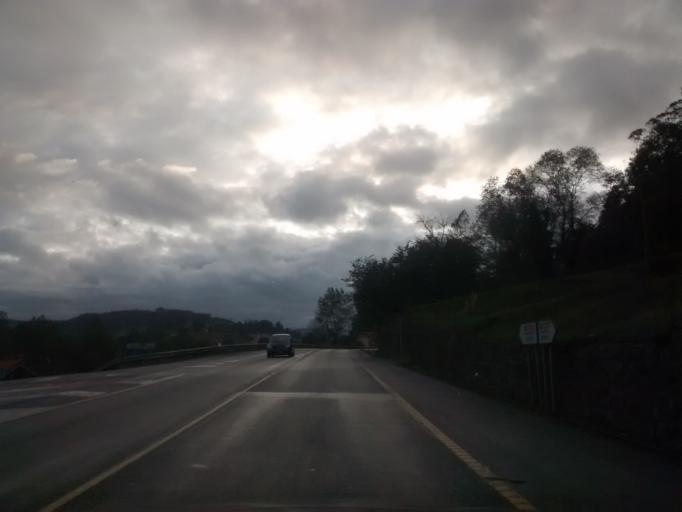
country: ES
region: Cantabria
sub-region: Provincia de Cantabria
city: Penagos
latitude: 43.3469
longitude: -3.7877
